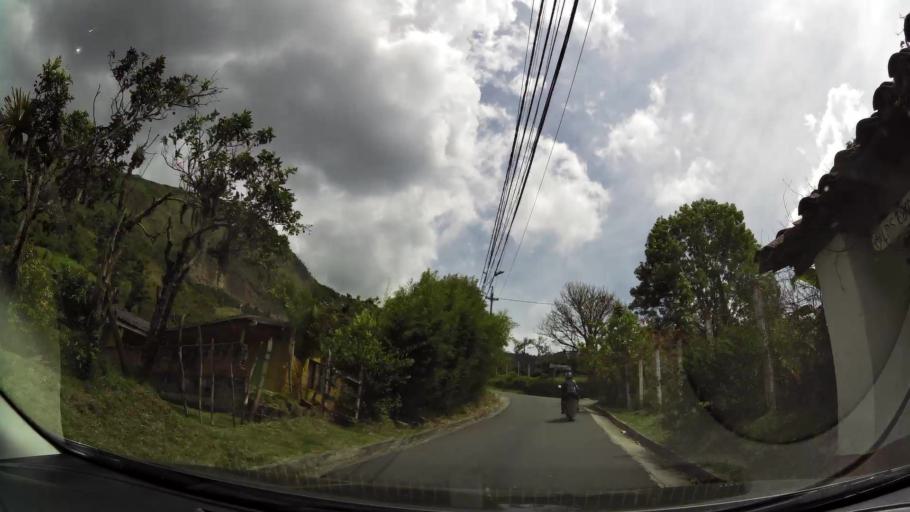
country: CO
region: Antioquia
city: Municipio de Copacabana
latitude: 6.3246
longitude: -75.4967
